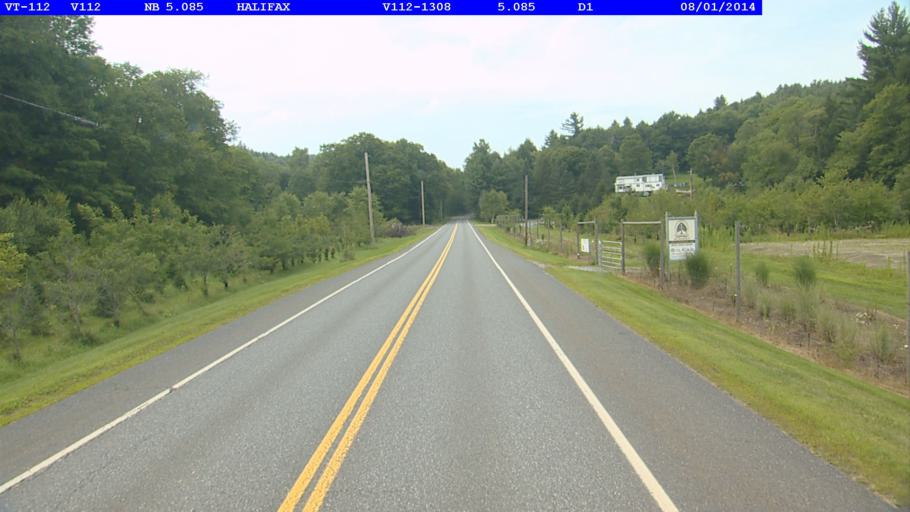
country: US
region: Massachusetts
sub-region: Franklin County
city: Colrain
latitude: 42.7692
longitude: -72.7988
